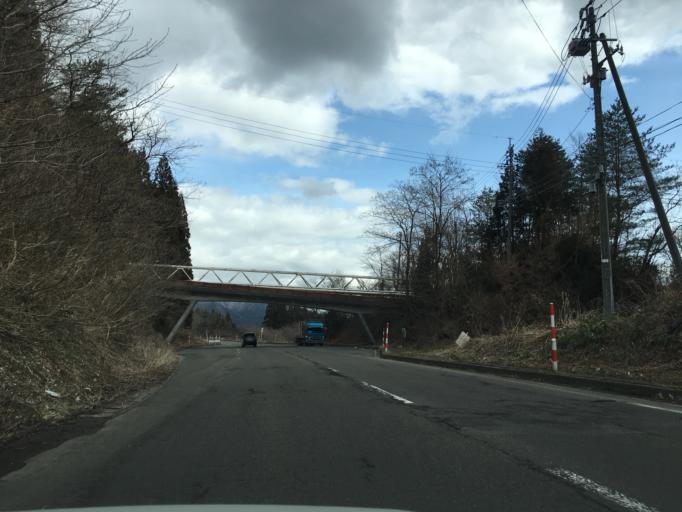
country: JP
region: Akita
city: Odate
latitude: 40.2184
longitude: 140.6434
